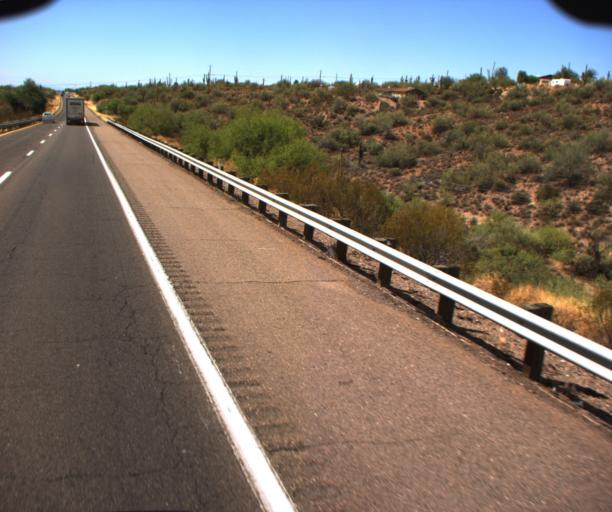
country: US
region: Arizona
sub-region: Maricopa County
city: New River
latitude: 33.9223
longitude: -112.1446
